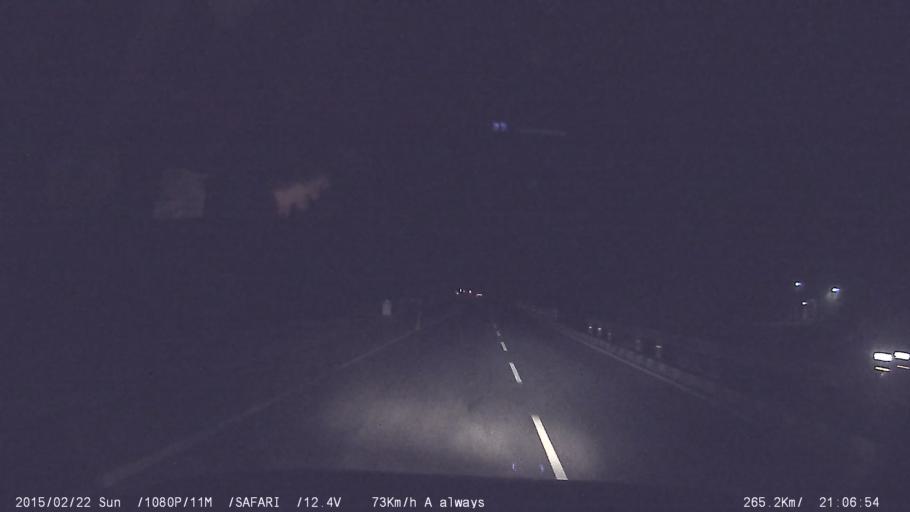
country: IN
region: Tamil Nadu
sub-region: Karur
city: Pallappatti
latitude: 10.7157
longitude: 77.9291
